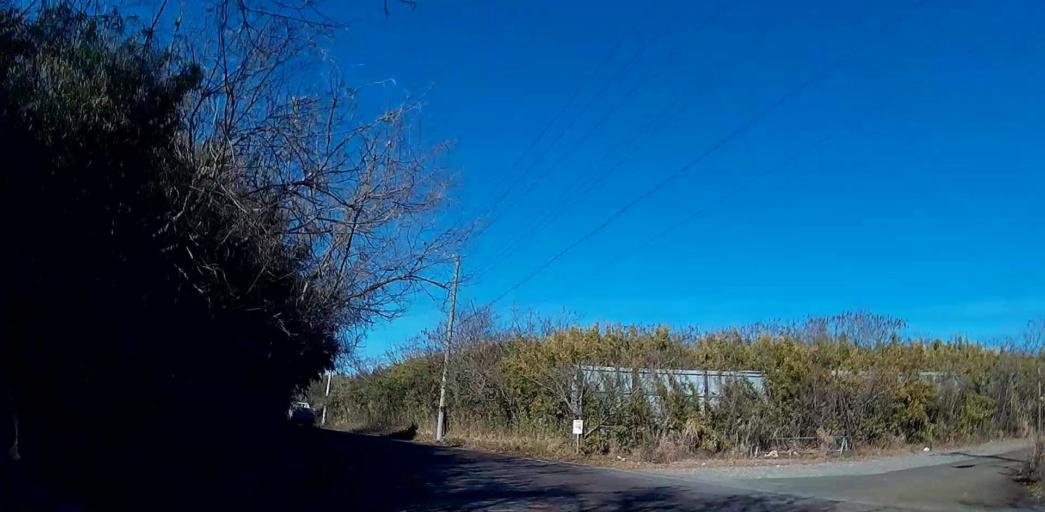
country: JP
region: Chiba
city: Narita
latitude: 35.7879
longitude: 140.3854
